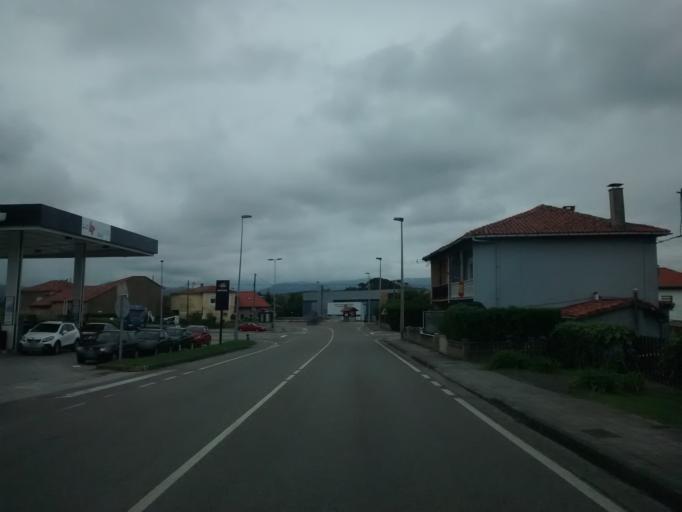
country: ES
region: Cantabria
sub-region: Provincia de Cantabria
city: Polanco
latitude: 43.3983
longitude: -4.0490
